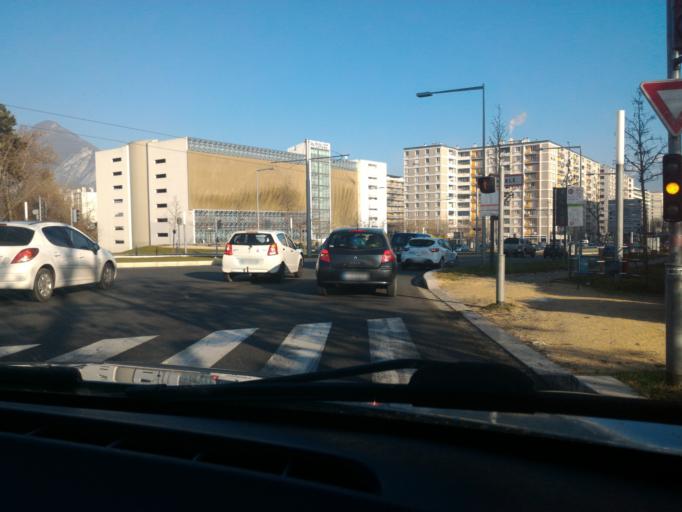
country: FR
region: Rhone-Alpes
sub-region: Departement de l'Isere
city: Seyssinet-Pariset
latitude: 45.1798
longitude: 5.7035
